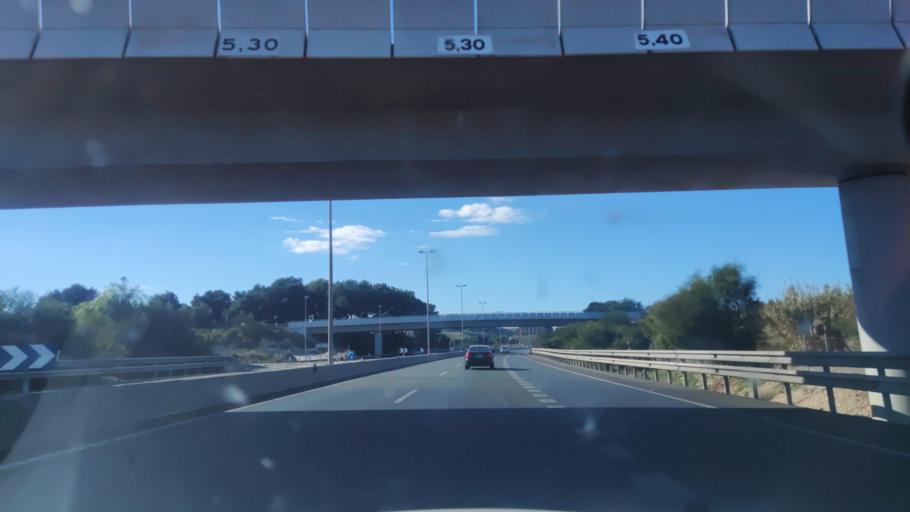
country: ES
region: Valencia
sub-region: Provincia de Alicante
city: San Juan de Alicante
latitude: 38.3812
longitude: -0.4593
